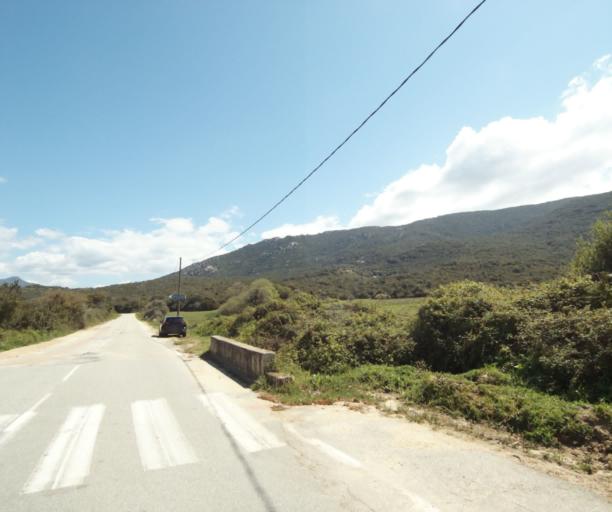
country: FR
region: Corsica
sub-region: Departement de la Corse-du-Sud
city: Propriano
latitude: 41.6448
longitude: 8.8692
